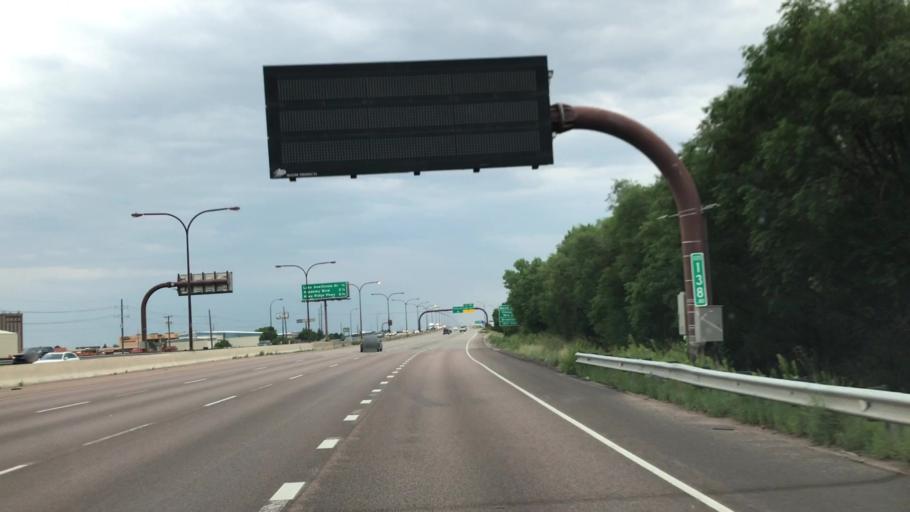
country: US
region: Colorado
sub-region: El Paso County
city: Stratmoor
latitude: 38.8026
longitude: -104.8010
